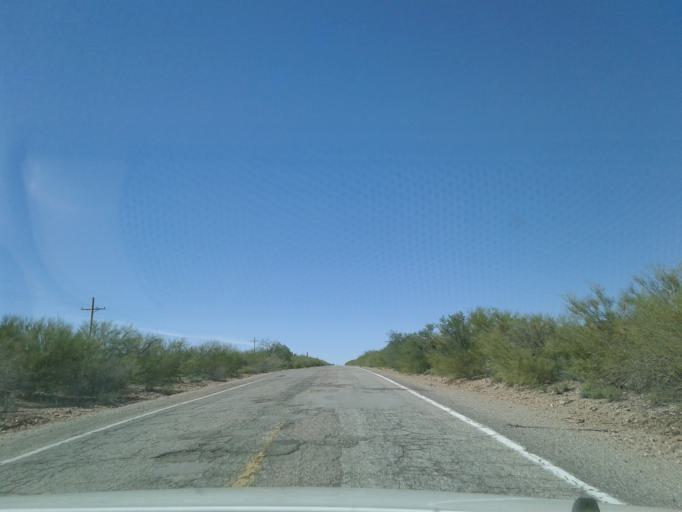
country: US
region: Arizona
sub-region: Pima County
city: Avra Valley
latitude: 32.3767
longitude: -111.4749
